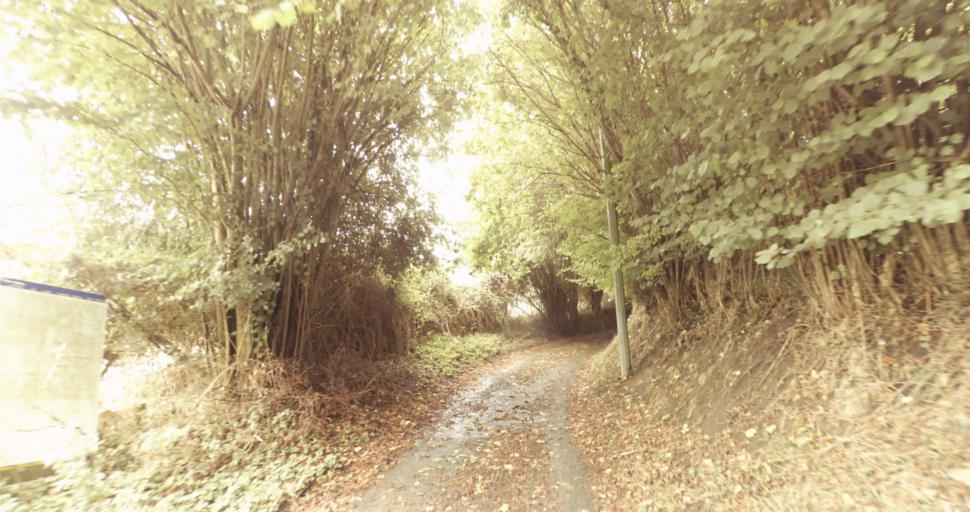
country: FR
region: Lower Normandy
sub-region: Departement de l'Orne
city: Vimoutiers
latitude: 48.8794
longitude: 0.1836
